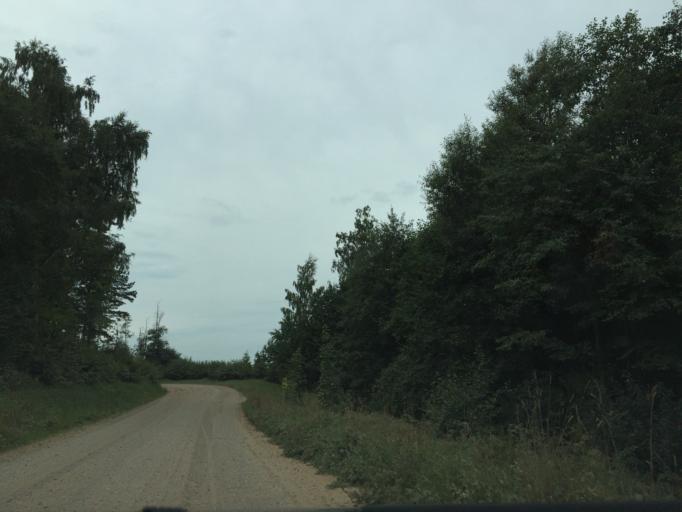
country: LV
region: Jaunpils
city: Jaunpils
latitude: 56.7489
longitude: 23.1218
